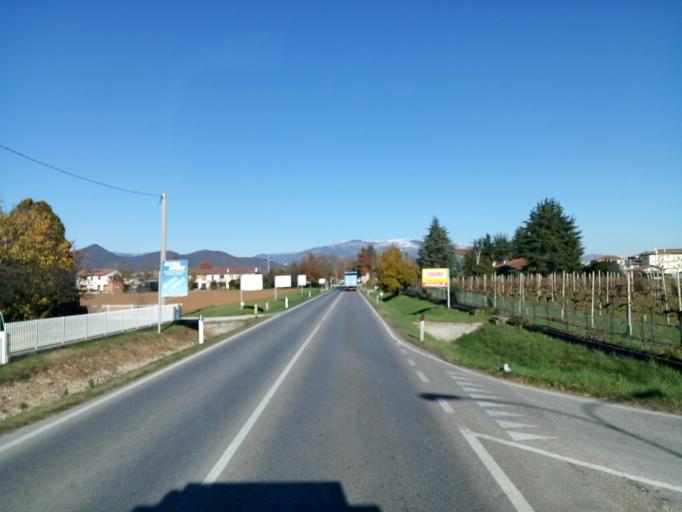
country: IT
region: Veneto
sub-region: Provincia di Treviso
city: Caerano di San Marco
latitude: 45.7835
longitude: 11.9938
